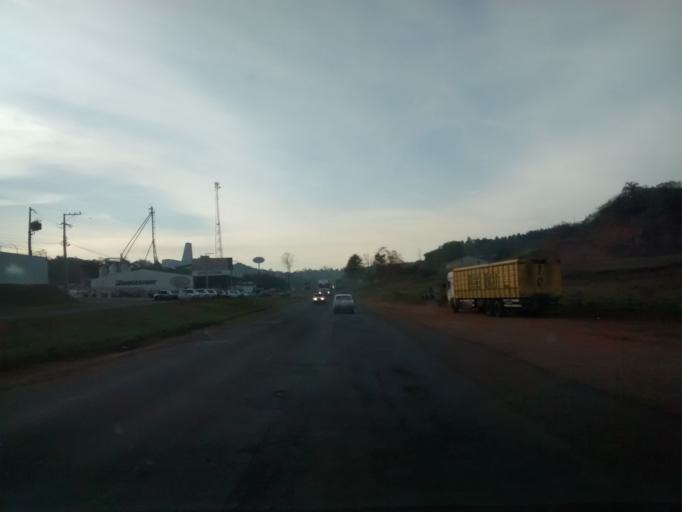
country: BR
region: Parana
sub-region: Francisco Beltrao
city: Francisco Beltrao
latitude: -26.1116
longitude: -53.0505
